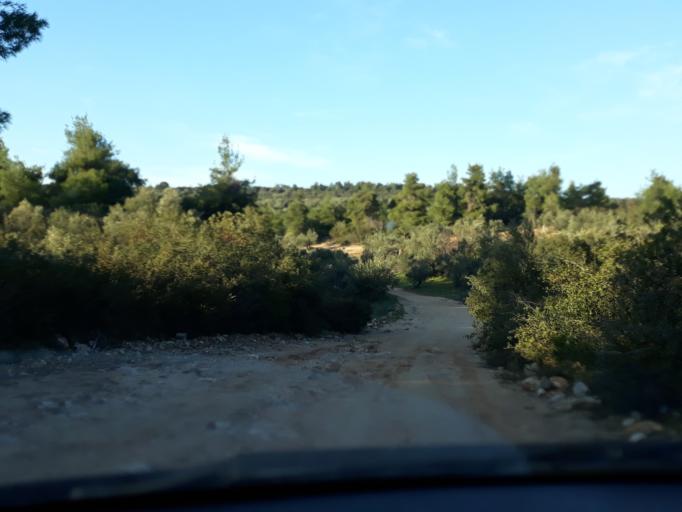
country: GR
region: Central Greece
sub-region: Nomos Voiotias
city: Asopia
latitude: 38.2631
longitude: 23.5352
